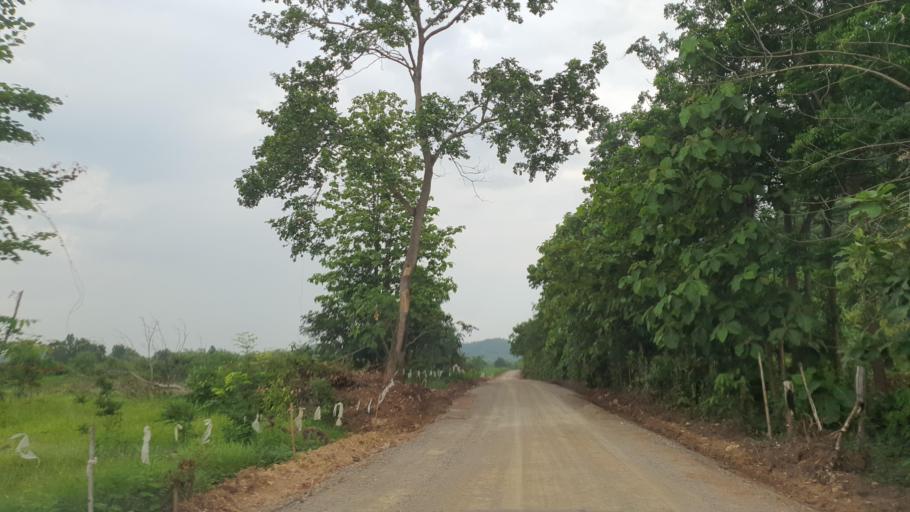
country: TH
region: Sukhothai
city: Thung Saliam
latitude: 17.2586
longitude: 99.5396
